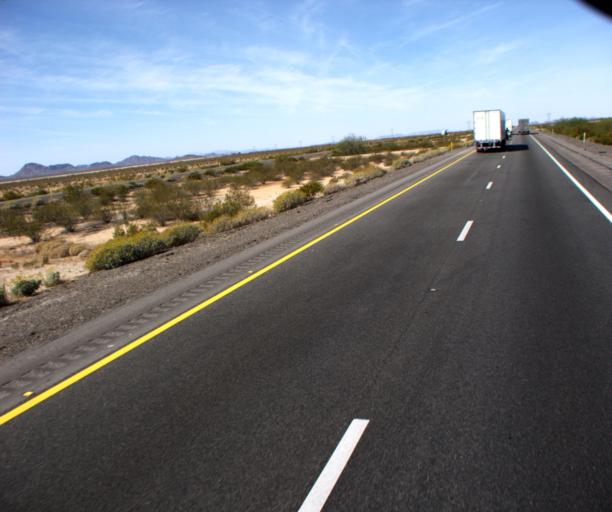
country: US
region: Arizona
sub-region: La Paz County
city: Salome
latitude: 33.5718
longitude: -113.3697
